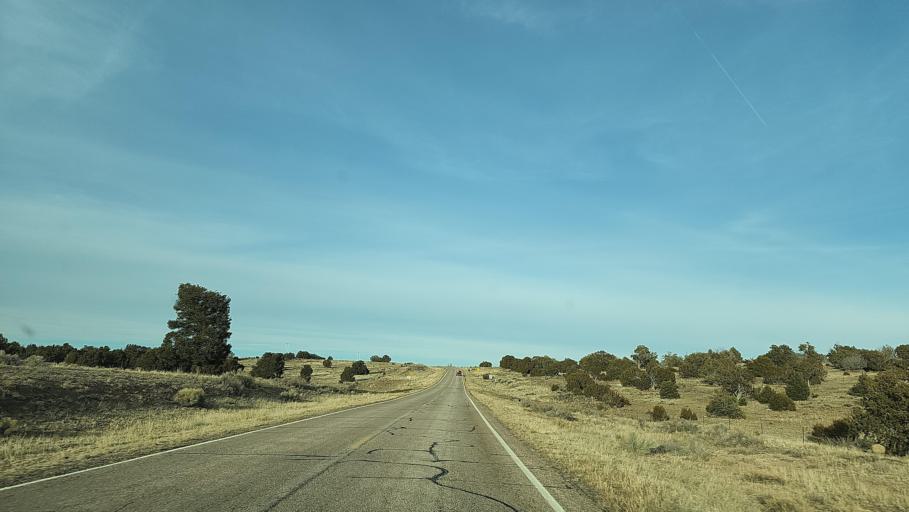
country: US
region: New Mexico
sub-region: Catron County
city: Reserve
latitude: 34.3860
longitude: -108.4529
